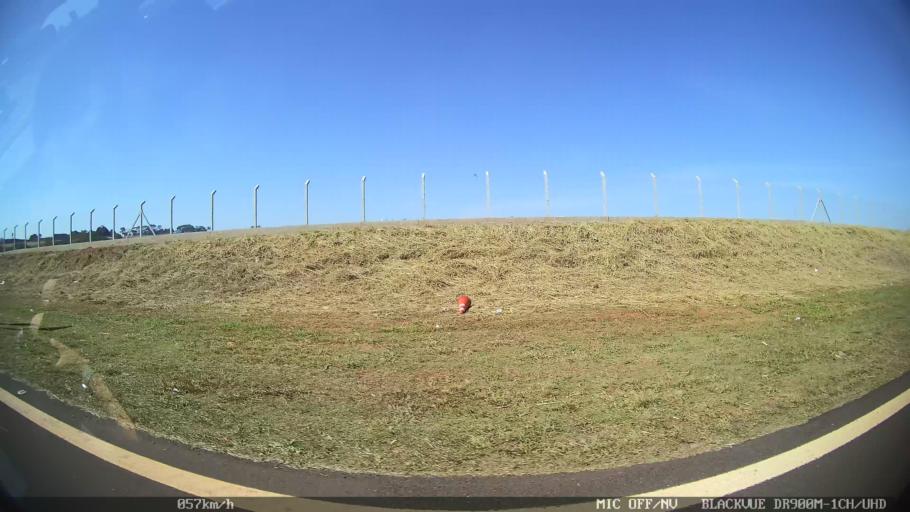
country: BR
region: Sao Paulo
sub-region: Batatais
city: Batatais
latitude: -20.8742
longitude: -47.6062
